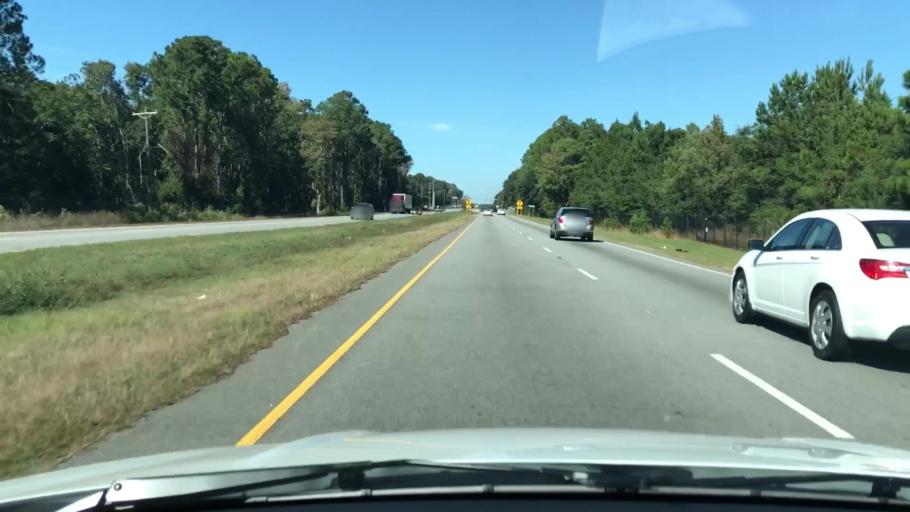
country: US
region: South Carolina
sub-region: Beaufort County
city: Burton
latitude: 32.4891
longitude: -80.7411
